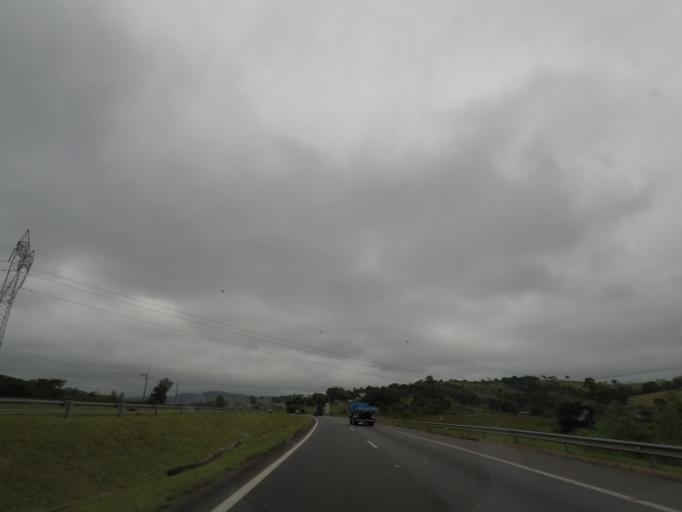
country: BR
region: Sao Paulo
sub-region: Bom Jesus Dos Perdoes
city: Bom Jesus dos Perdoes
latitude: -23.1713
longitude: -46.4250
